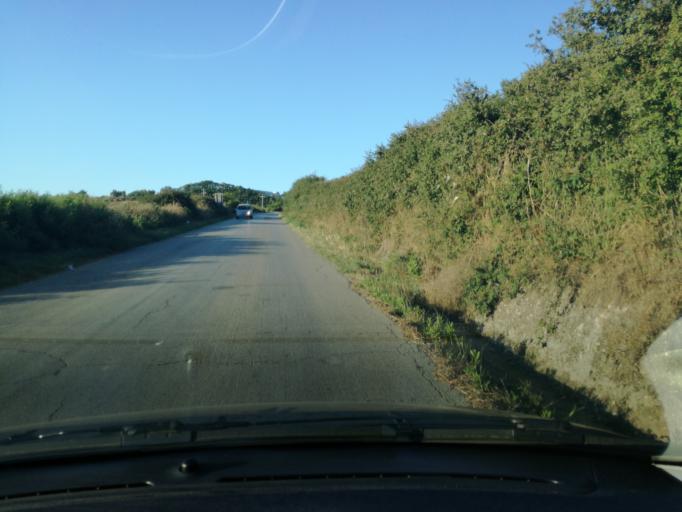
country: IT
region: Molise
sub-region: Provincia di Campobasso
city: Guglionesi
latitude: 41.9331
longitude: 14.9414
